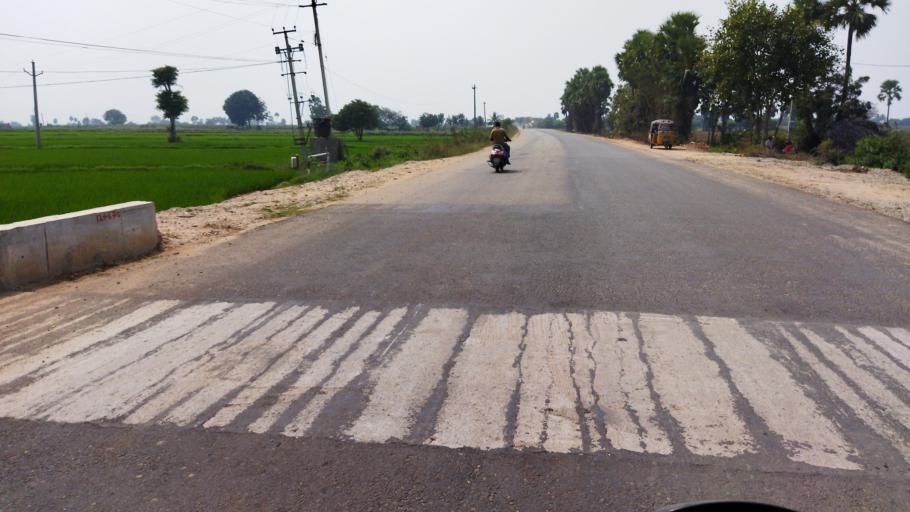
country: IN
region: Telangana
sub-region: Nalgonda
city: Nalgonda
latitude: 17.0965
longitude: 79.3363
